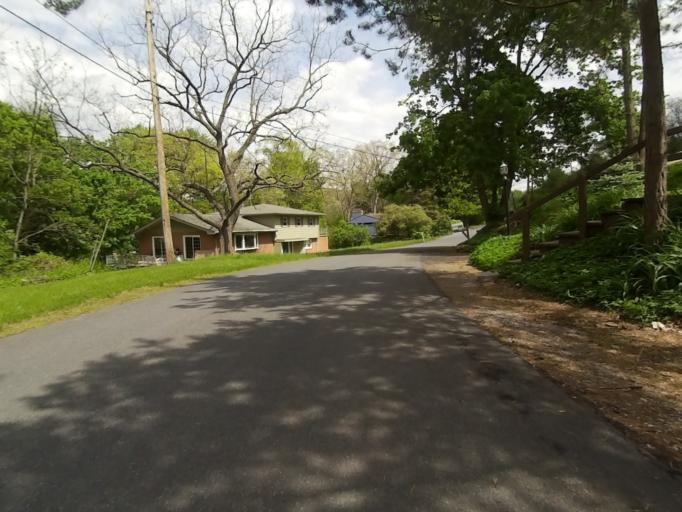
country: US
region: Pennsylvania
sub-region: Centre County
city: Houserville
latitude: 40.8118
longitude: -77.8414
